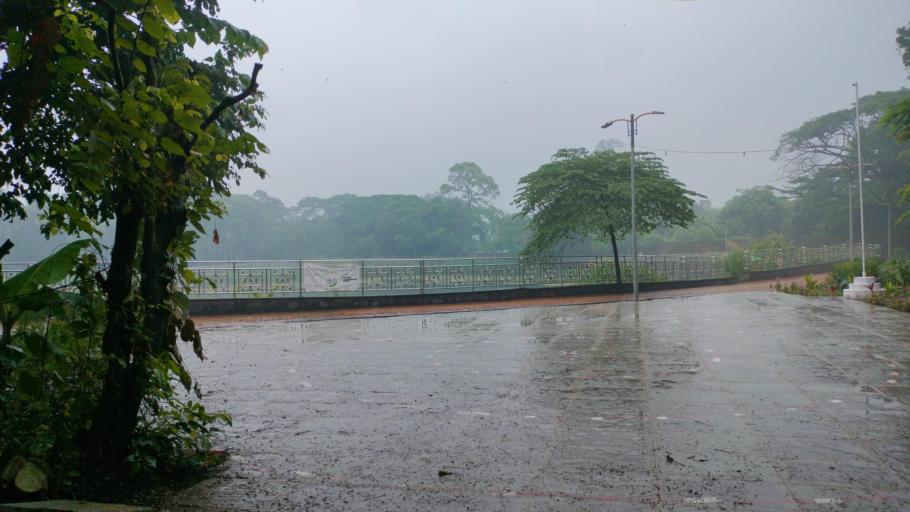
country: IN
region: Maharashtra
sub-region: Mumbai Suburban
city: Powai
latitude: 19.1260
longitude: 72.8797
